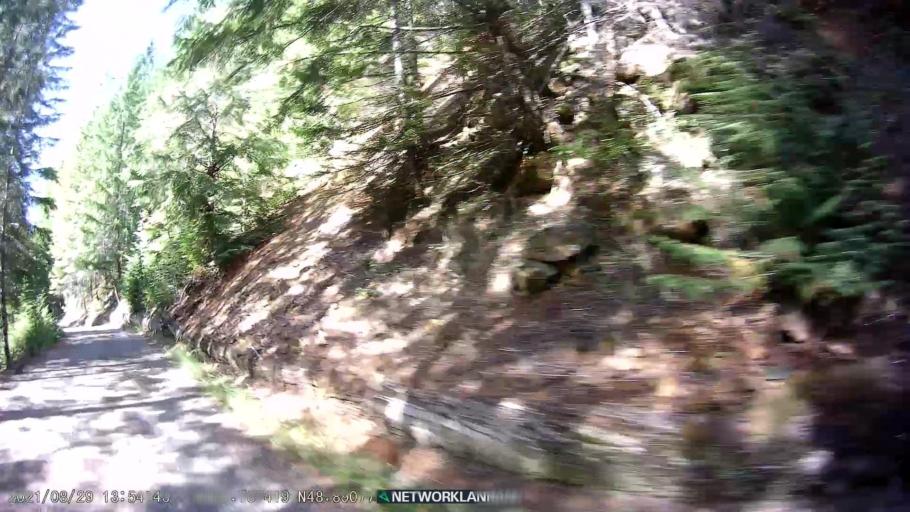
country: CA
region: British Columbia
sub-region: Fraser Valley Regional District
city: Chilliwack
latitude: 48.8908
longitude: -121.7876
